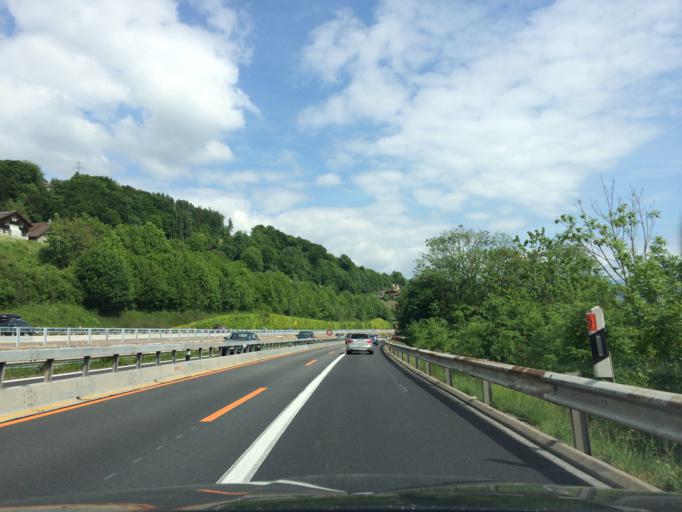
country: CH
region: Vaud
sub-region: Lavaux-Oron District
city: Chexbres
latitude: 46.4817
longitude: 6.7880
